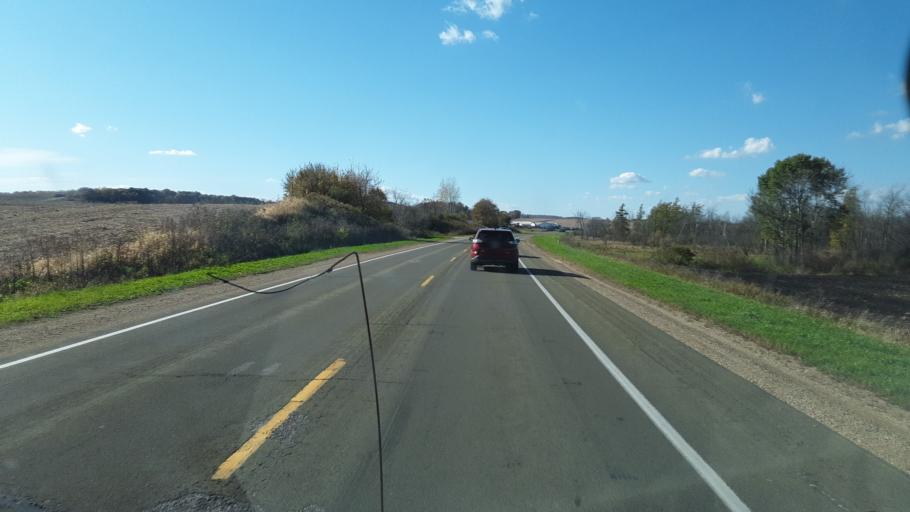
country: US
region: Wisconsin
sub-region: Sauk County
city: Reedsburg
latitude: 43.5427
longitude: -90.0430
